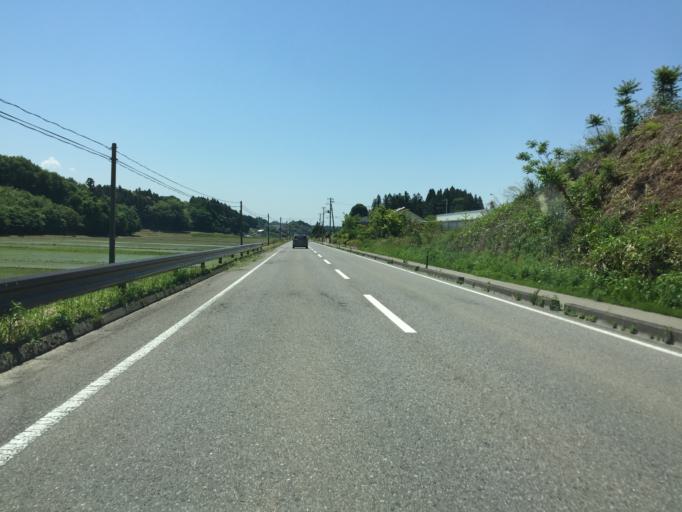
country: JP
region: Fukushima
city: Motomiya
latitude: 37.5074
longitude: 140.4581
